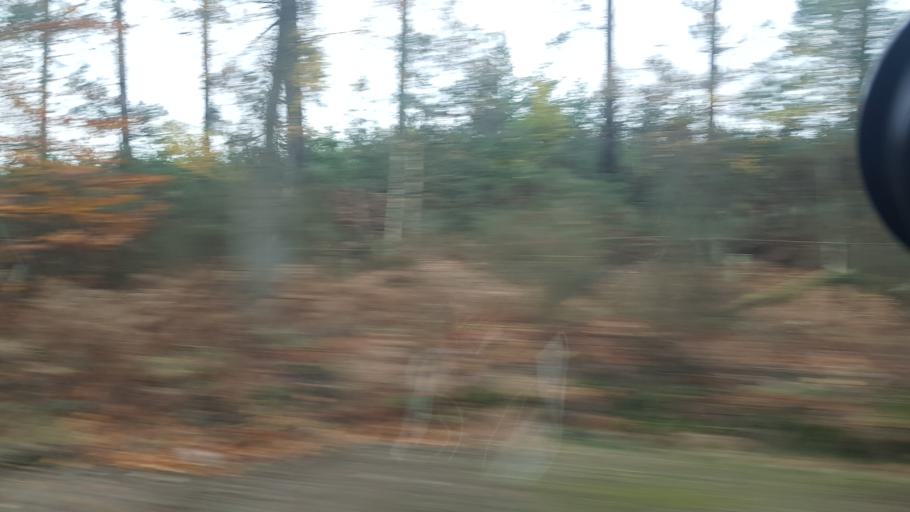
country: GB
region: England
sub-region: Hampshire
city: Eversley
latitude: 51.3220
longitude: -0.8693
